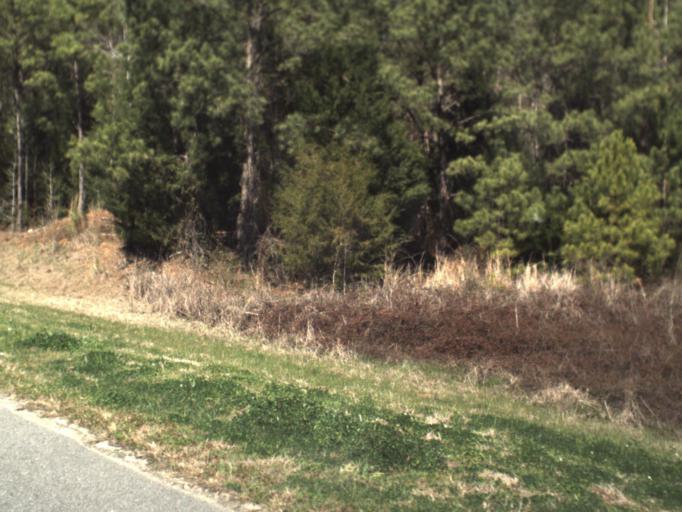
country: US
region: Florida
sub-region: Jackson County
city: Marianna
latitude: 30.7979
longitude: -85.2727
